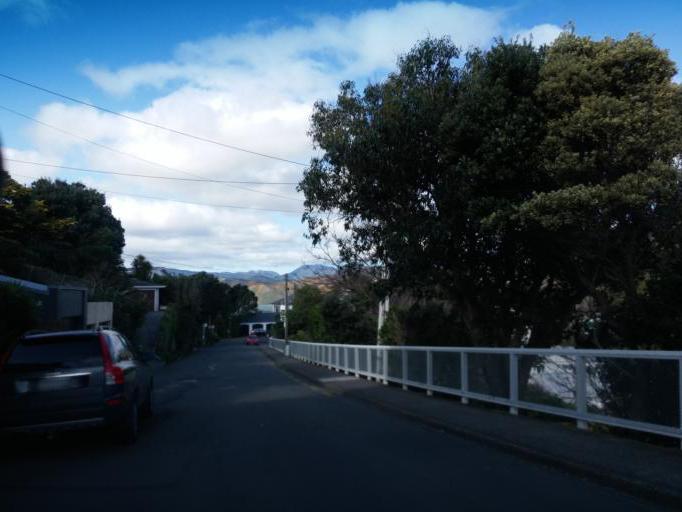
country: NZ
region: Wellington
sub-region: Wellington City
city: Wellington
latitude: -41.3232
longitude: 174.8261
